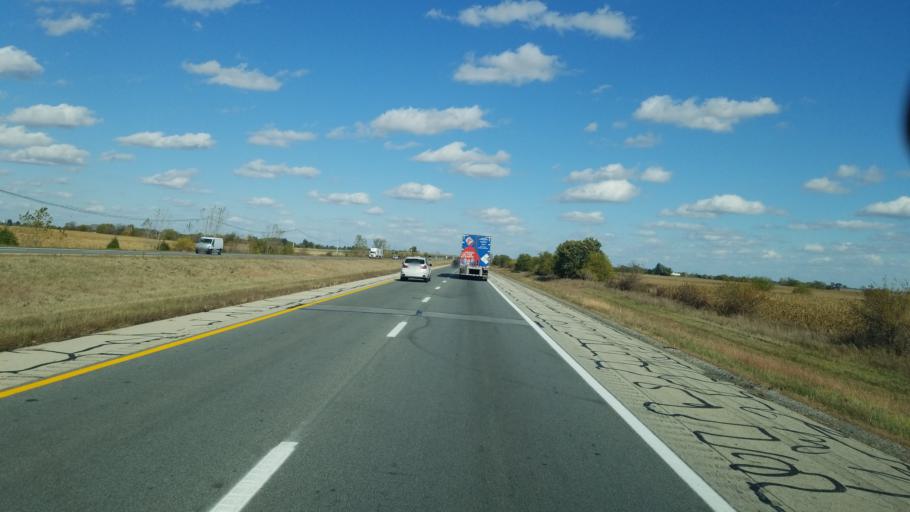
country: US
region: Ohio
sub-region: Fayette County
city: Jeffersonville
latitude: 39.6777
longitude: -83.4908
